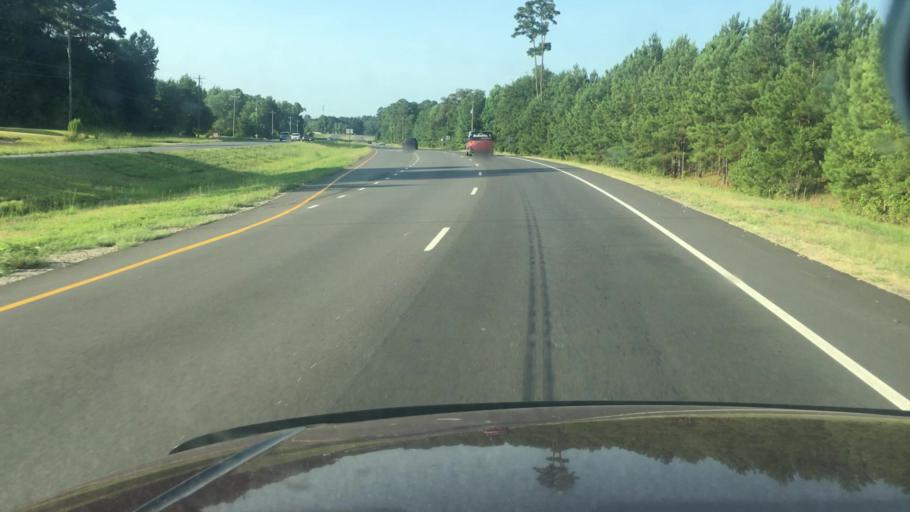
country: US
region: North Carolina
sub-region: Cumberland County
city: Hope Mills
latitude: 34.9452
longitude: -78.8472
